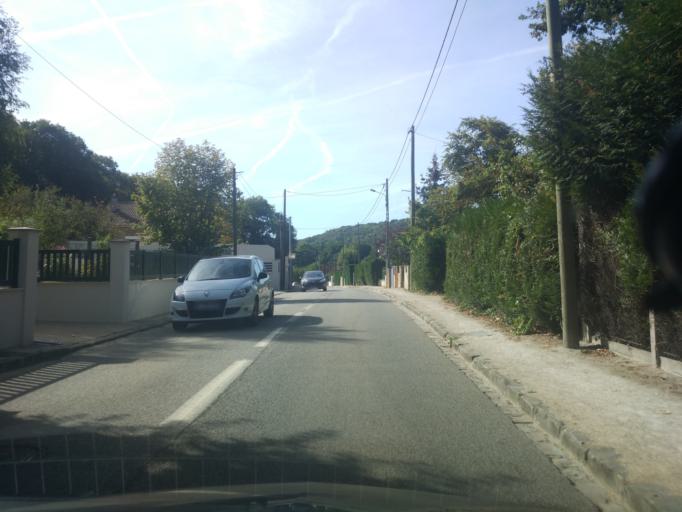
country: FR
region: Ile-de-France
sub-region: Departement des Yvelines
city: Saint-Remy-les-Chevreuse
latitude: 48.6983
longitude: 2.0677
